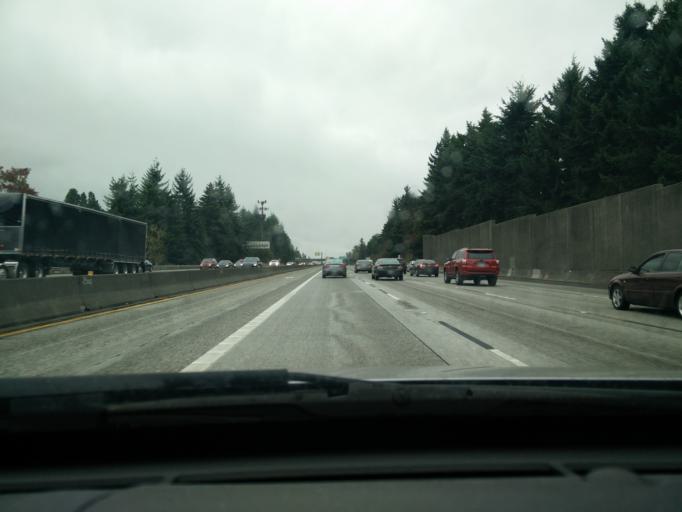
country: US
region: Washington
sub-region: King County
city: Shoreline
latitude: 47.7284
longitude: -122.3244
